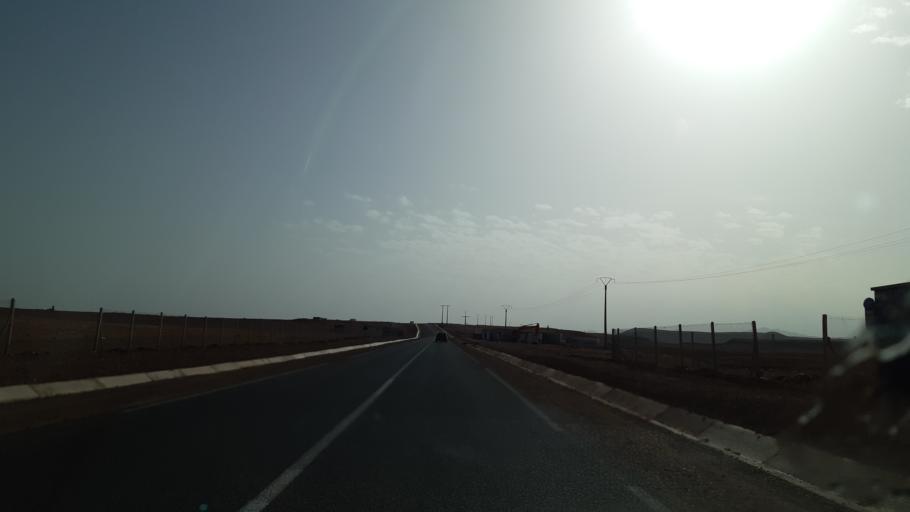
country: MA
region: Meknes-Tafilalet
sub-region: Khenifra
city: Itzer
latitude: 32.8658
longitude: -4.9140
